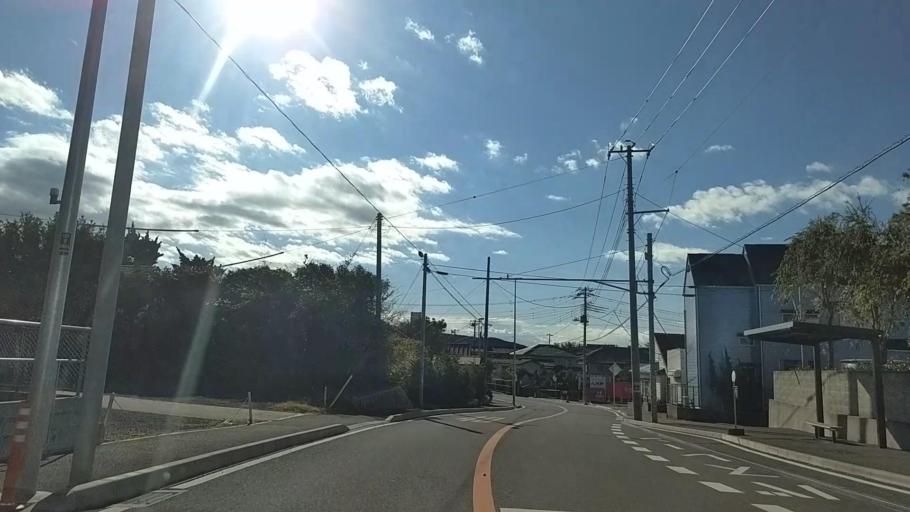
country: JP
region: Chiba
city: Tateyama
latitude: 35.0479
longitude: 139.8350
